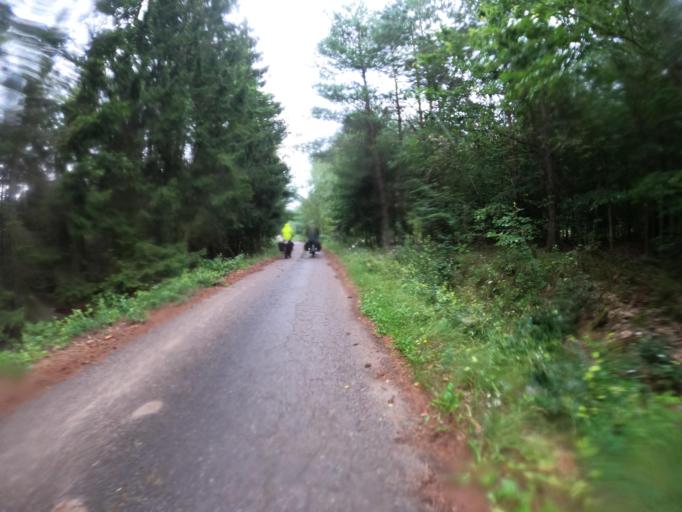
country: PL
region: West Pomeranian Voivodeship
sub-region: Powiat szczecinecki
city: Grzmiaca
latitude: 53.7127
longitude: 16.4939
